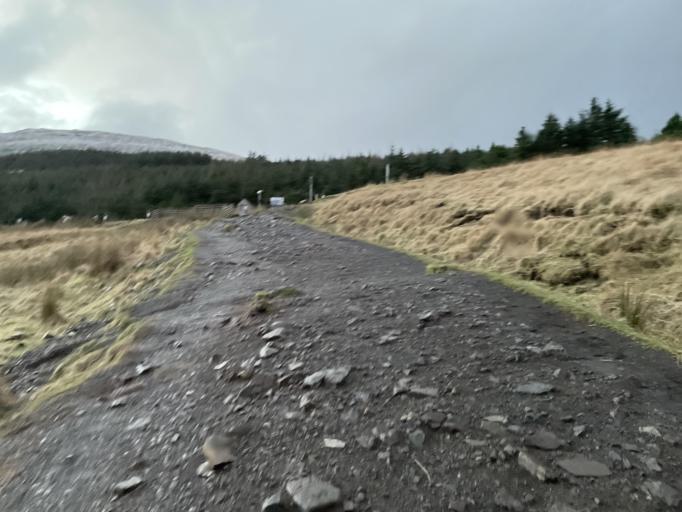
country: GB
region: Scotland
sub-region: Highland
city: Isle of Skye
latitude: 57.2507
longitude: -6.2713
